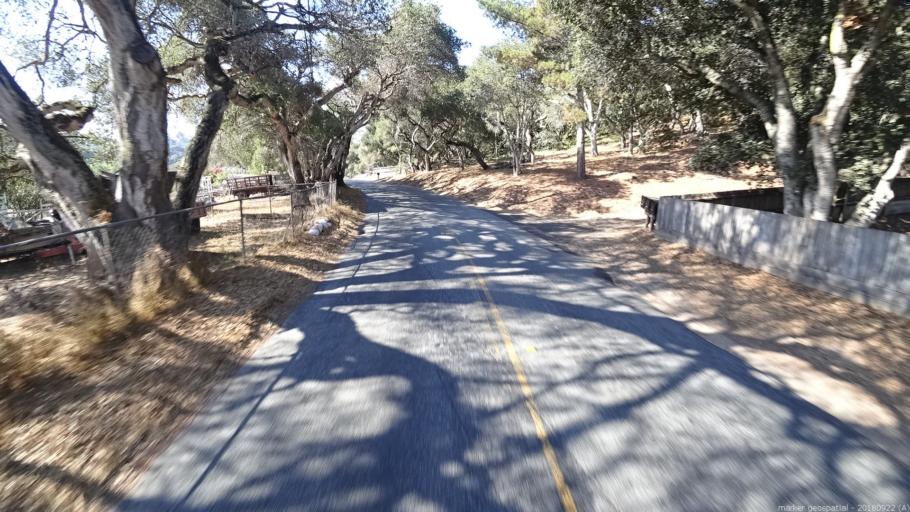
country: US
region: California
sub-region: Monterey County
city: Prunedale
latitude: 36.8143
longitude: -121.6428
